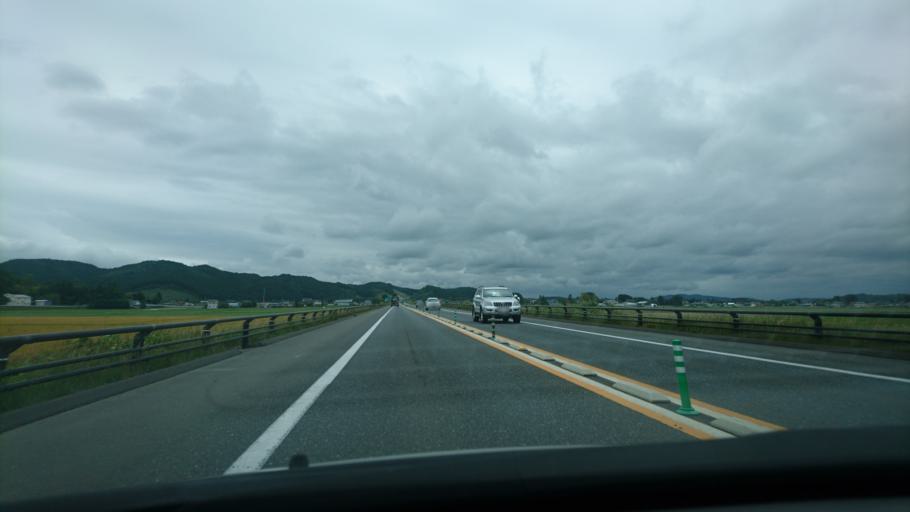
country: JP
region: Miyagi
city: Wakuya
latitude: 38.6154
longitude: 141.2848
